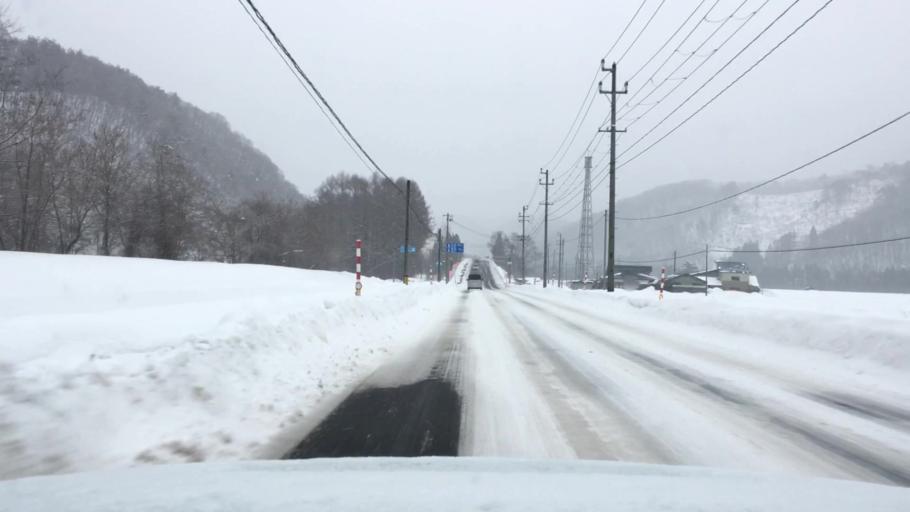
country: JP
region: Akita
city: Hanawa
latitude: 40.0595
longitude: 141.0123
